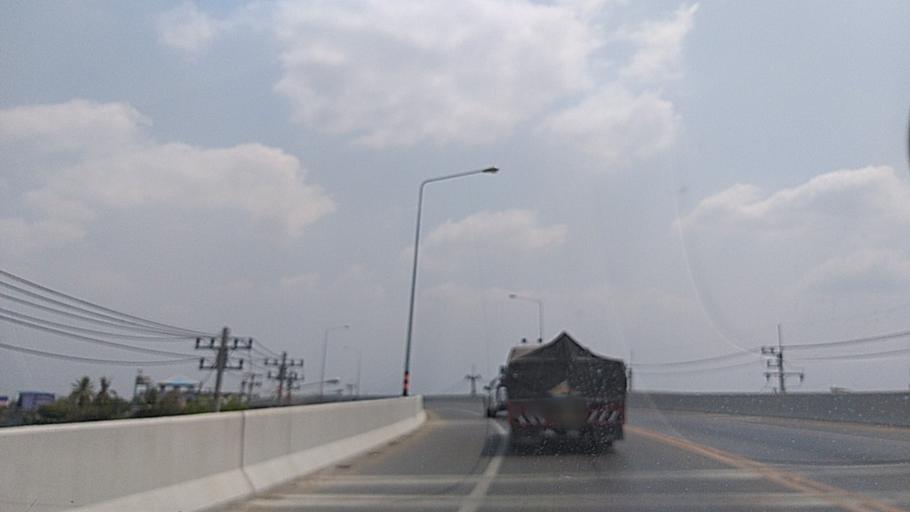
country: TH
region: Chachoengsao
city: Chachoengsao
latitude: 13.7456
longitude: 101.0794
